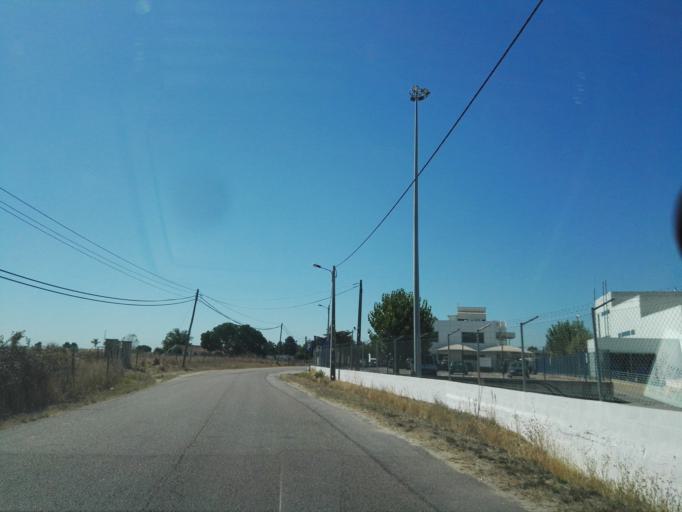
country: PT
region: Santarem
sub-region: Benavente
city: Samora Correia
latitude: 38.9124
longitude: -8.8653
